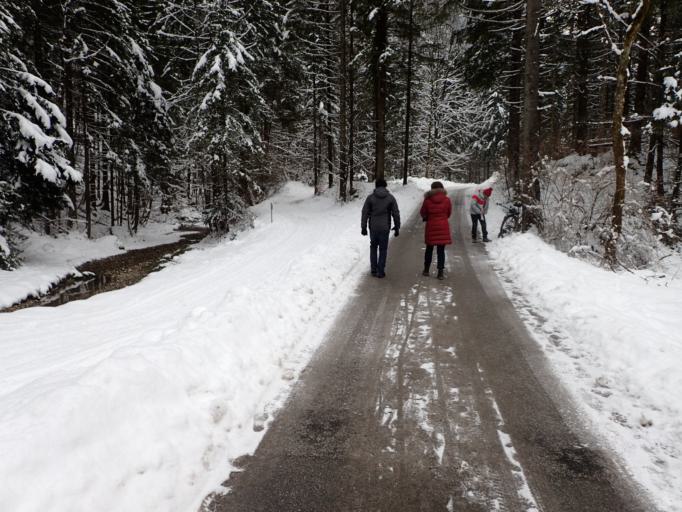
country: AT
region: Salzburg
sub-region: Politischer Bezirk Hallein
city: Golling an der Salzach
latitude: 47.5826
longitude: 13.1496
